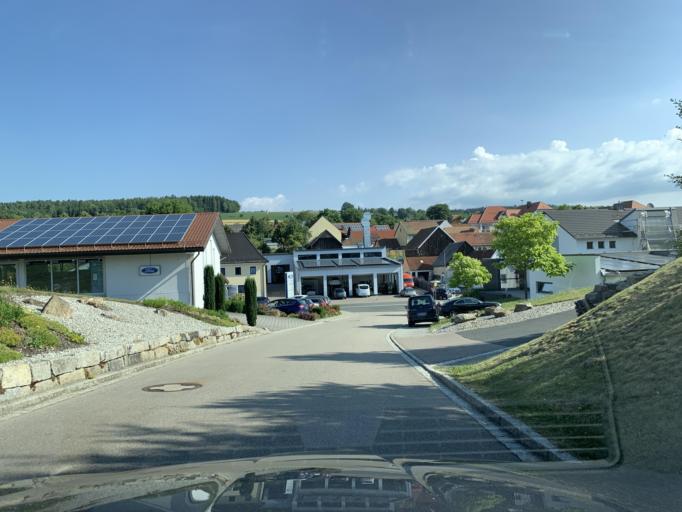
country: DE
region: Bavaria
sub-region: Upper Palatinate
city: Dieterskirchen
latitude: 49.4128
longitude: 12.4128
